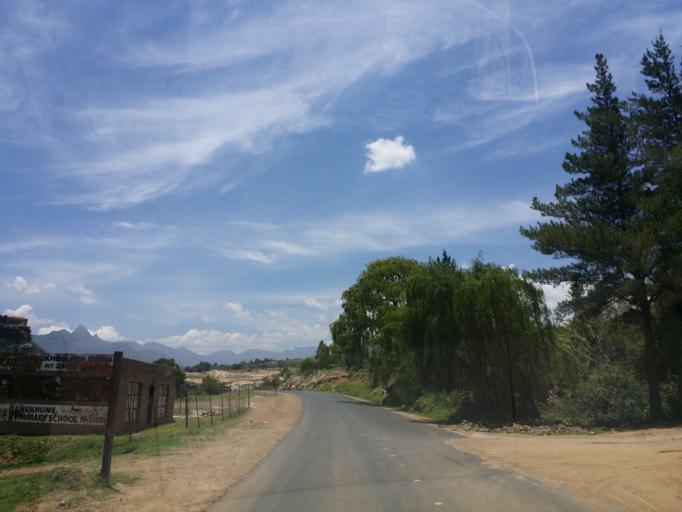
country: LS
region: Butha-Buthe
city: Butha-Buthe
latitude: -28.7356
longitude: 28.4130
